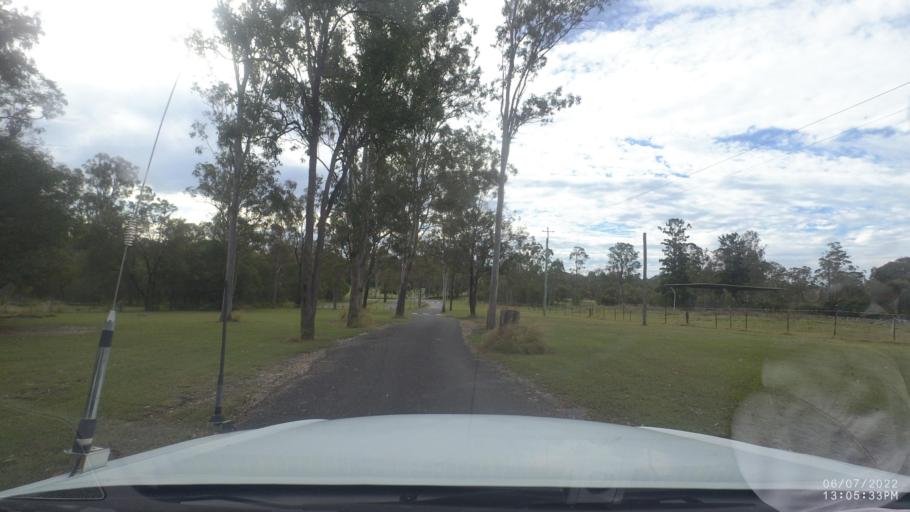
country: AU
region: Queensland
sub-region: Logan
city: Cedar Vale
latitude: -27.8480
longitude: 153.0293
